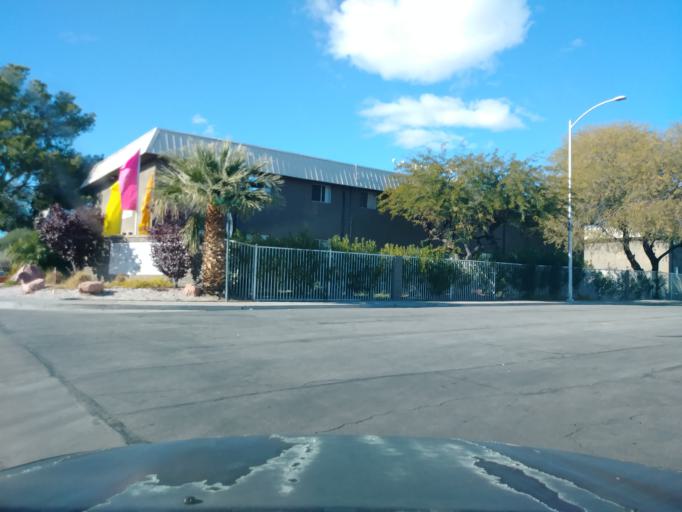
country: US
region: Nevada
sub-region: Clark County
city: Spring Valley
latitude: 36.1482
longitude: -115.2102
